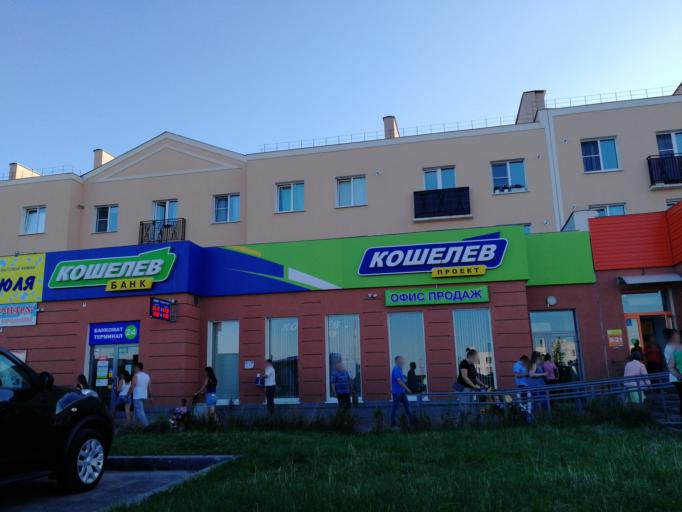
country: RU
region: Kaluga
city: Mstikhino
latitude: 54.4966
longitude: 36.1827
